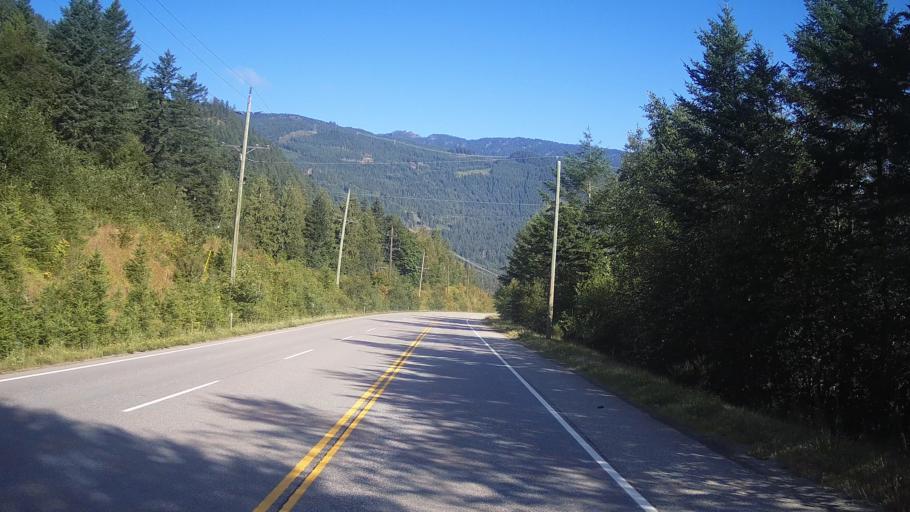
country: CA
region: British Columbia
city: Hope
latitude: 49.5340
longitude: -121.4273
